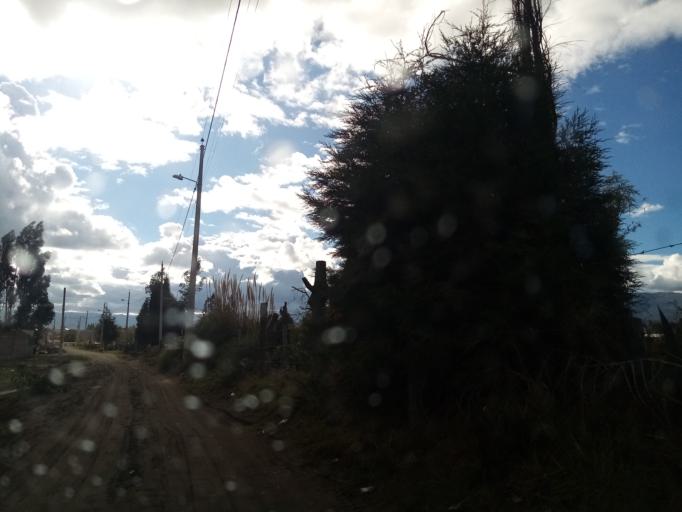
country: EC
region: Chimborazo
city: Riobamba
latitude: -1.6865
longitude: -78.6232
